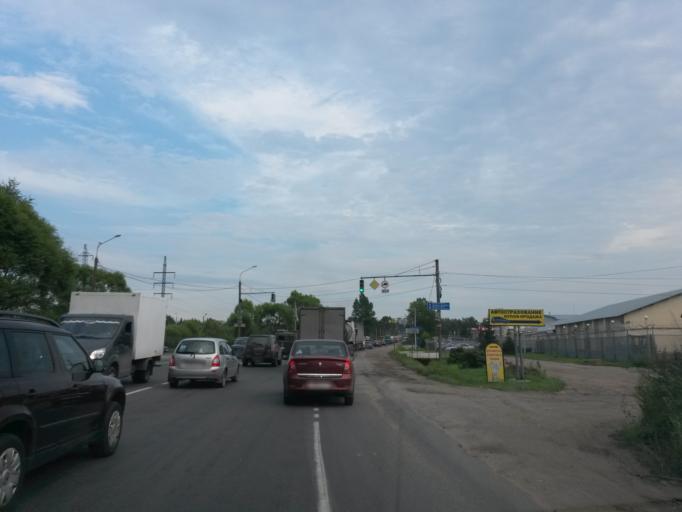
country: RU
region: Jaroslavl
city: Yaroslavl
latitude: 57.5958
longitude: 39.8108
